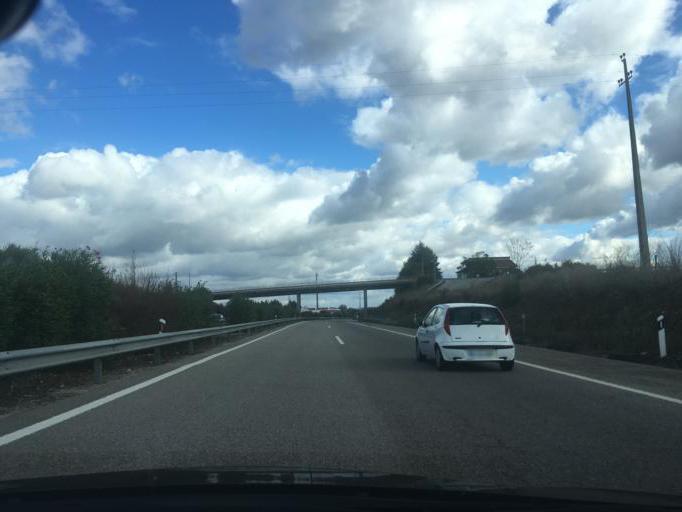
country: PT
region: Santarem
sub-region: Torres Novas
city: Torres Novas
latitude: 39.4720
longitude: -8.5831
